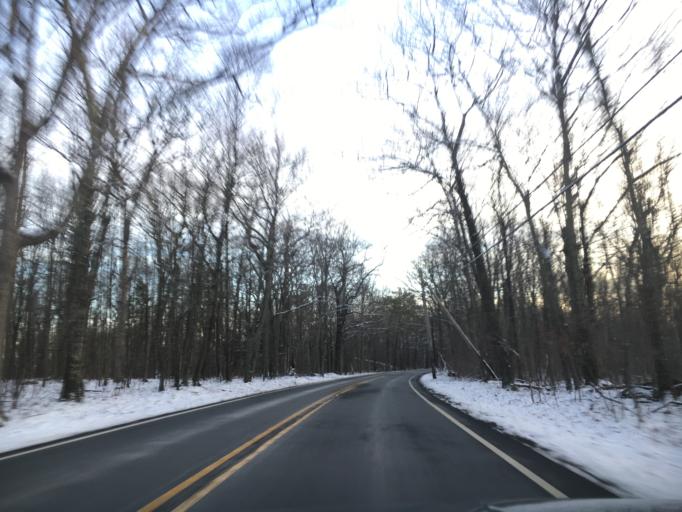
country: US
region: Pennsylvania
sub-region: Pike County
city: Saw Creek
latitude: 41.1505
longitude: -75.0801
